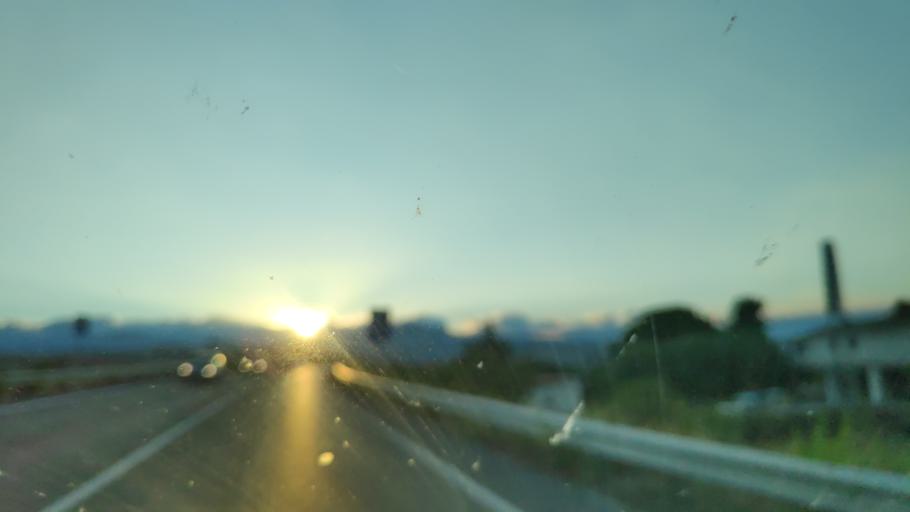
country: IT
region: Calabria
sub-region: Provincia di Reggio Calabria
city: Marina di Gioiosa Ionica
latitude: 38.2934
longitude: 16.3166
